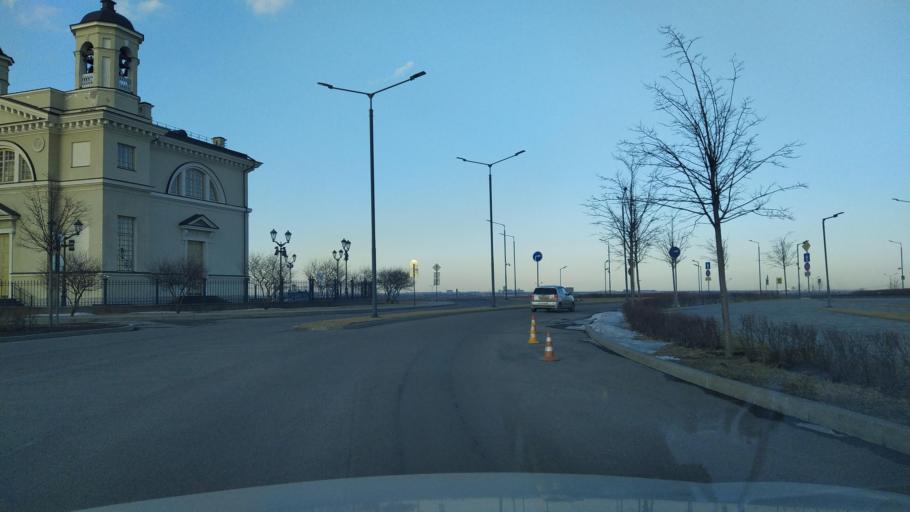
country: RU
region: St.-Petersburg
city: Aleksandrovskaya
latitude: 59.7645
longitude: 30.3503
